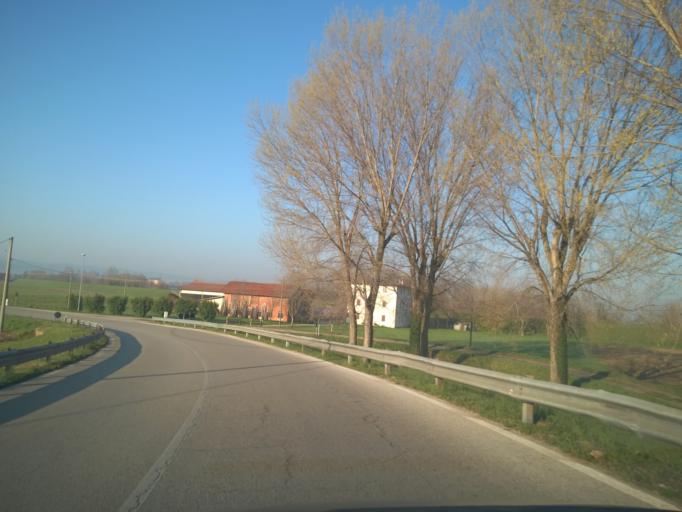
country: IT
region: Veneto
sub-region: Provincia di Vicenza
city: Marola
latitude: 45.5344
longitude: 11.6231
